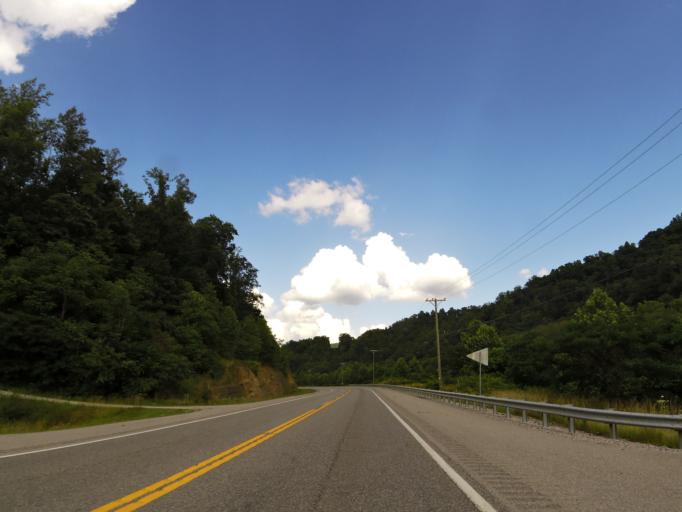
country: US
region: Kentucky
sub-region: Harlan County
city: Harlan
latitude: 36.8147
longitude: -83.2846
